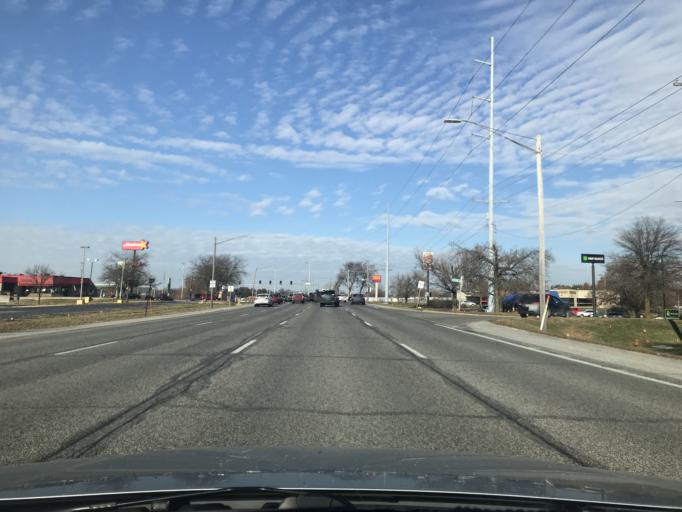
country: US
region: Iowa
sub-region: Scott County
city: Davenport
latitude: 41.5730
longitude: -90.5693
